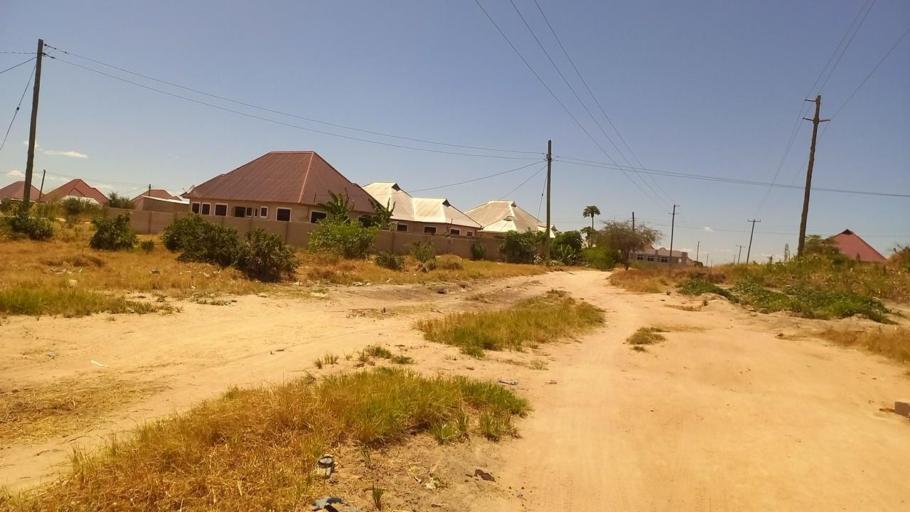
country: TZ
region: Dodoma
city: Dodoma
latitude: -6.1343
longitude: 35.7140
